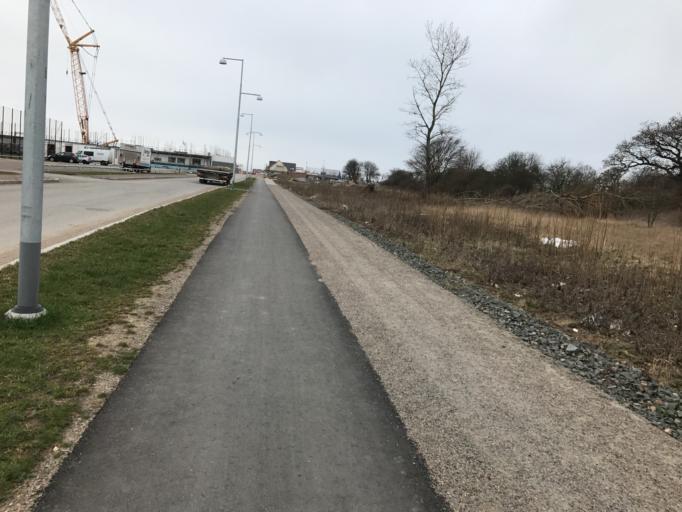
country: SE
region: Skane
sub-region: Landskrona
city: Landskrona
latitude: 55.9002
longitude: 12.8104
